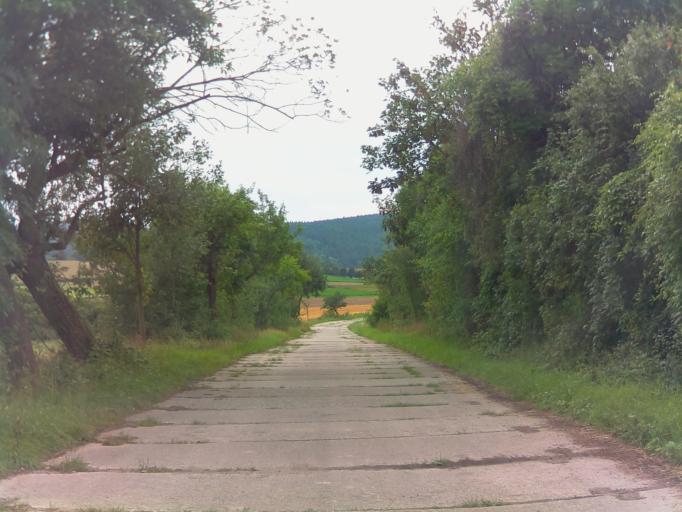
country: DE
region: Thuringia
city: Rittersdorf
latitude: 50.7678
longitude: 11.2845
